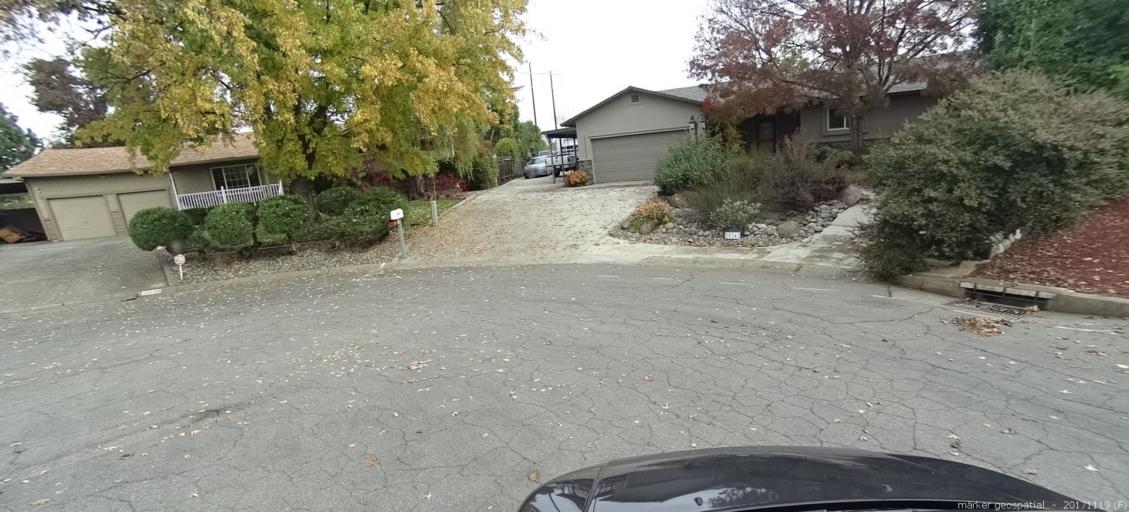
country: US
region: California
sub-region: Shasta County
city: Anderson
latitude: 40.4944
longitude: -122.3066
